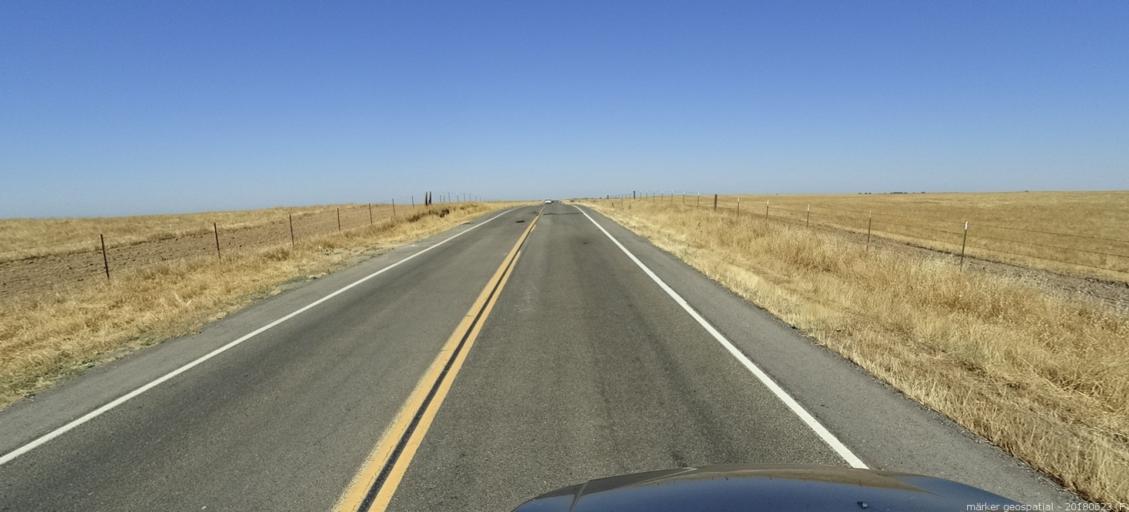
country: US
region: California
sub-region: Madera County
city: Bonadelle Ranchos-Madera Ranchos
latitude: 36.9667
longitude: -119.8356
